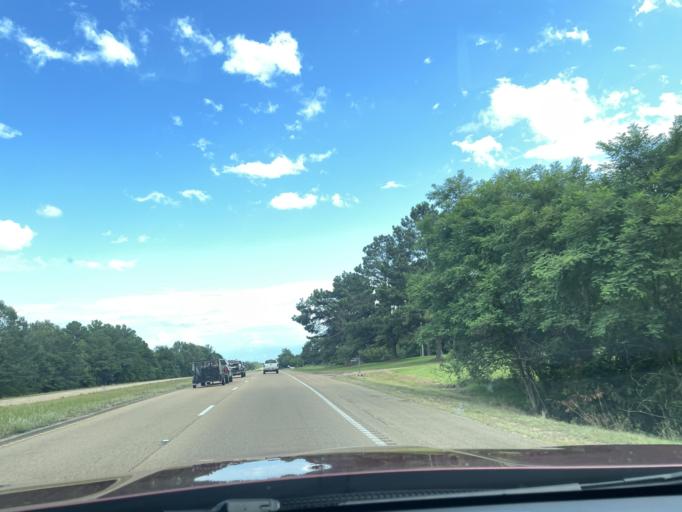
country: US
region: Mississippi
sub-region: Madison County
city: Flora
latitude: 32.5145
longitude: -90.3050
